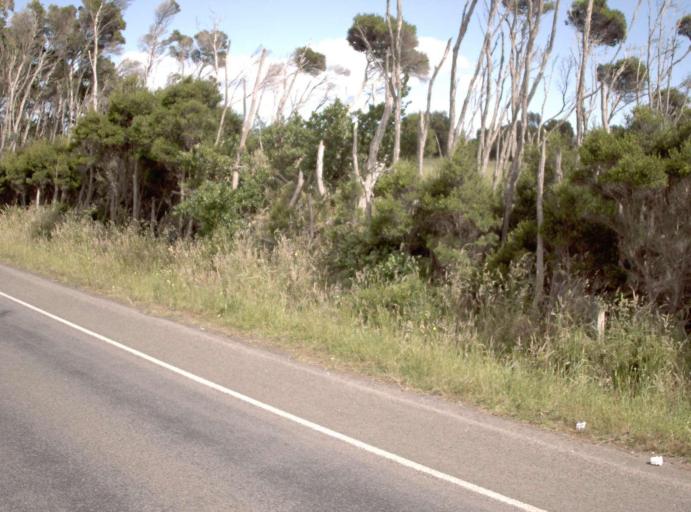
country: AU
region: Victoria
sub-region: Bass Coast
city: Phillip Island
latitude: -38.4967
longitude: 145.2318
